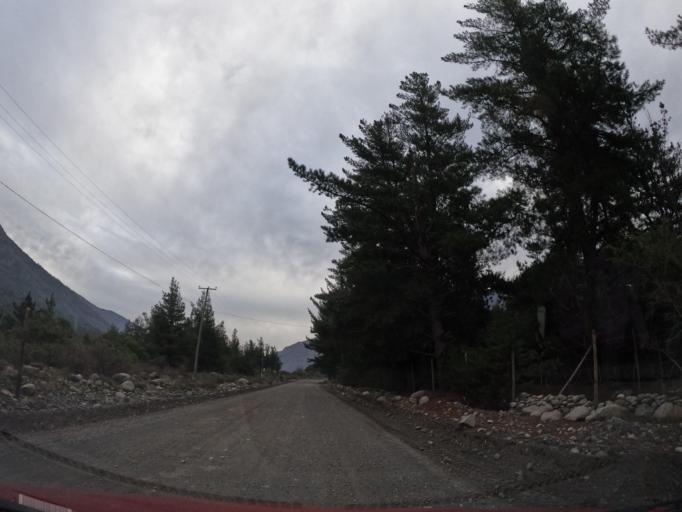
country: CL
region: Maule
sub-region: Provincia de Linares
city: Colbun
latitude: -35.7045
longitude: -71.0888
